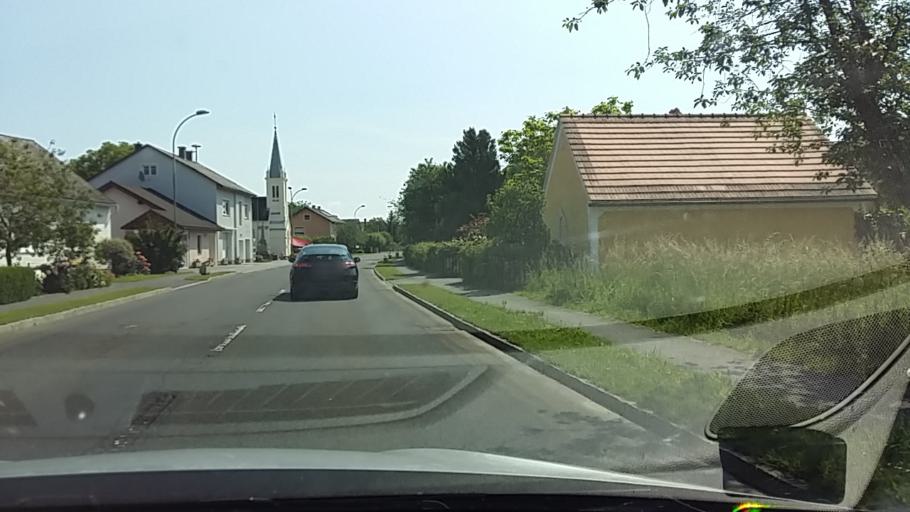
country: AT
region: Burgenland
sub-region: Politischer Bezirk Jennersdorf
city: Weichselbaum
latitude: 46.9413
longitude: 16.1852
